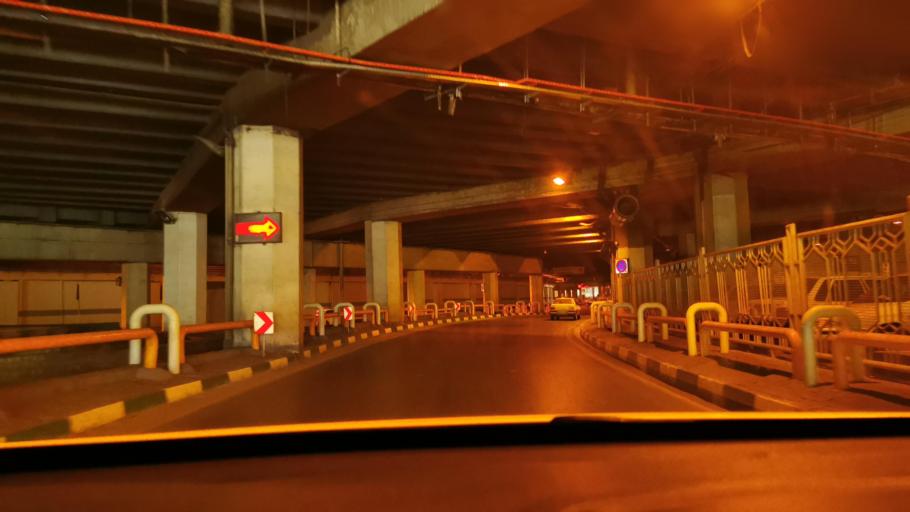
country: IR
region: Razavi Khorasan
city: Mashhad
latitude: 36.2867
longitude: 59.6181
